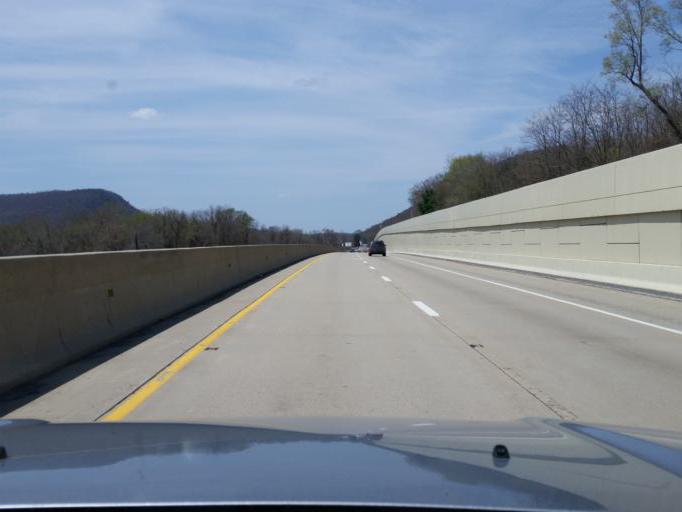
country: US
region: Pennsylvania
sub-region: Perry County
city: Duncannon
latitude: 40.3731
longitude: -76.9950
